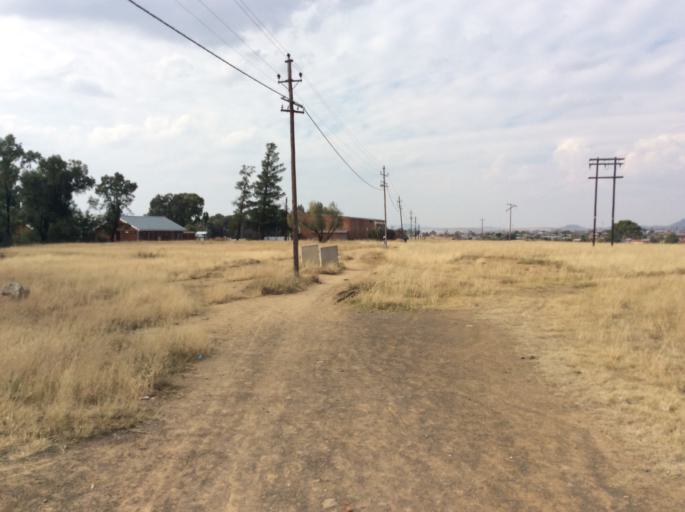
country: ZA
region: Orange Free State
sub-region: Xhariep District Municipality
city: Dewetsdorp
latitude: -29.5799
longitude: 26.6738
